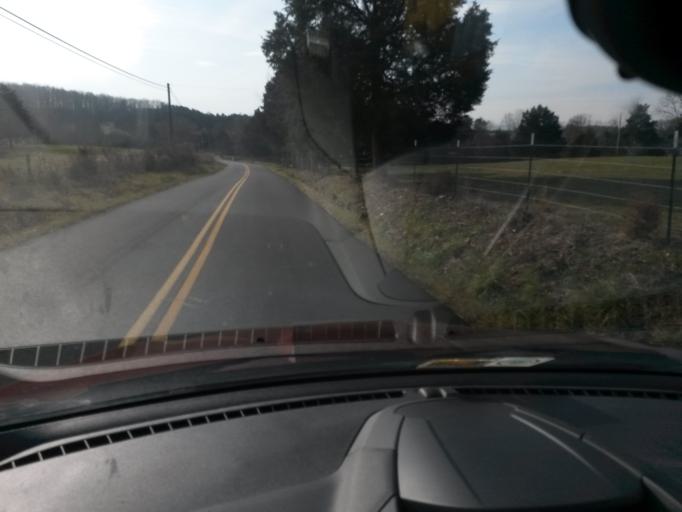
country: US
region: Virginia
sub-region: Botetourt County
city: Fincastle
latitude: 37.5398
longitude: -79.8754
